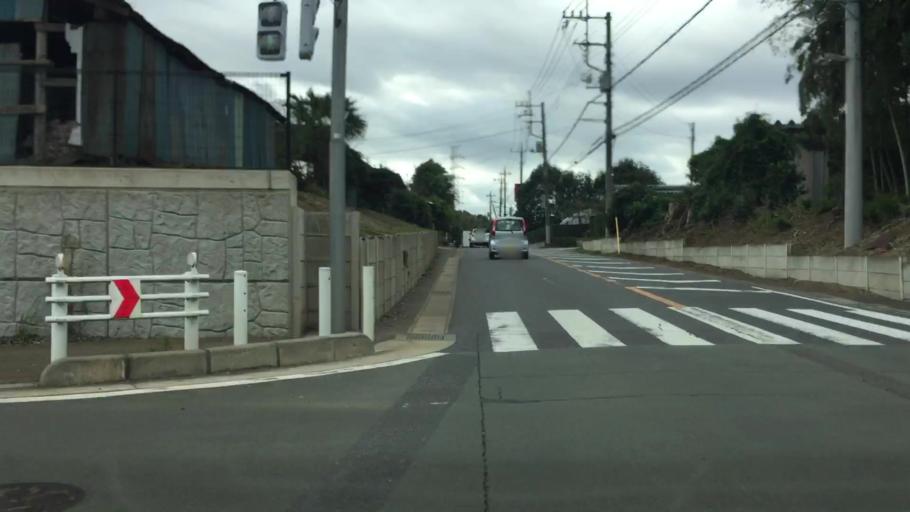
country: JP
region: Chiba
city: Shiroi
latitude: 35.8119
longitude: 140.1324
